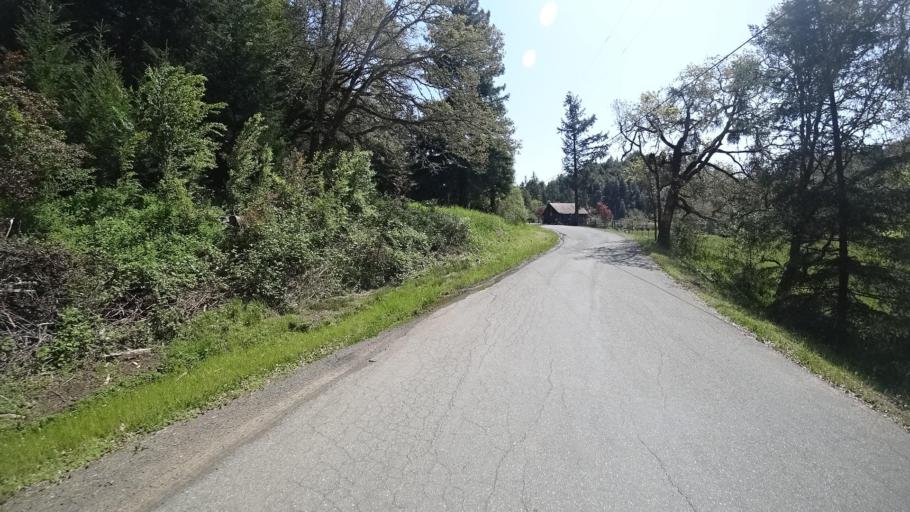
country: US
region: California
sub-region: Humboldt County
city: Redway
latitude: 40.2786
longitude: -123.6405
